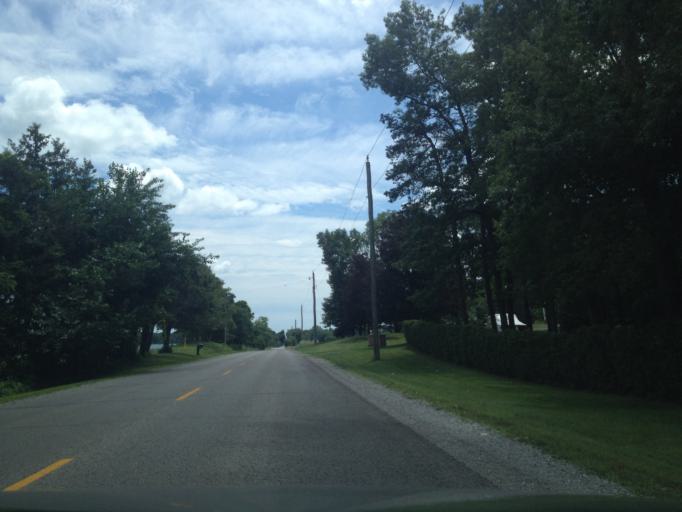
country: CA
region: Ontario
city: Norfolk County
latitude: 42.8148
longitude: -80.3241
